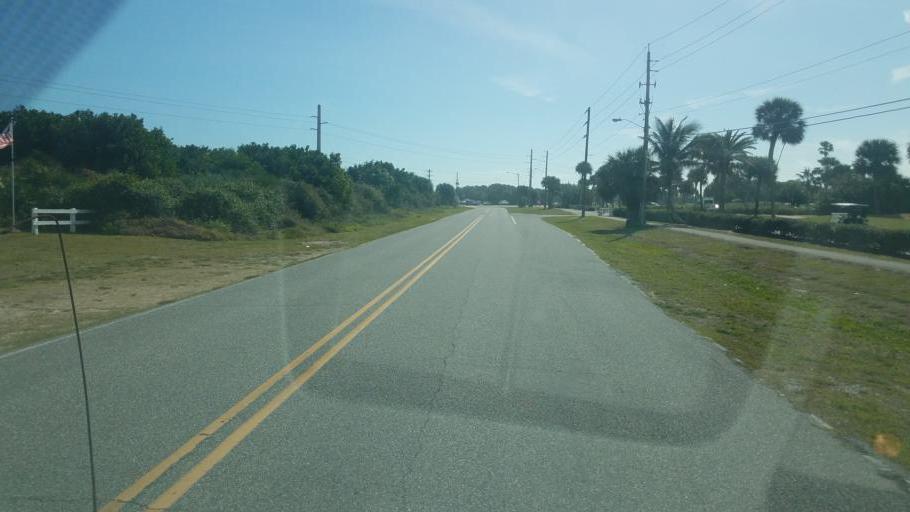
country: US
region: Florida
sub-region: Brevard County
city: Melbourne Beach
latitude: 28.0510
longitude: -80.5506
